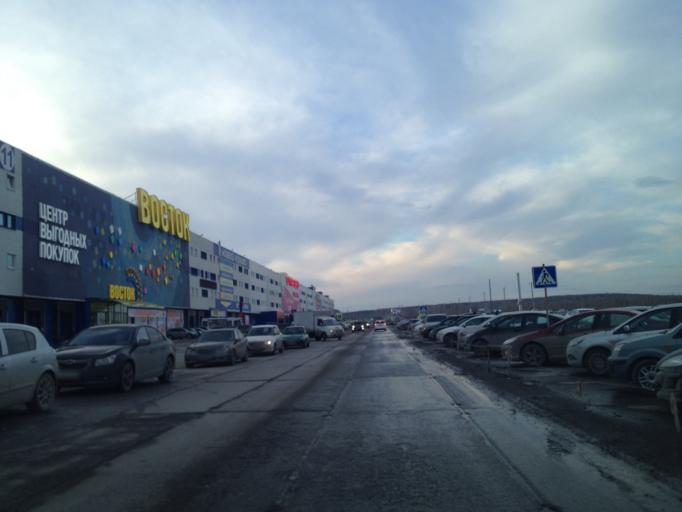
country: RU
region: Sverdlovsk
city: Istok
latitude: 56.7599
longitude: 60.7543
